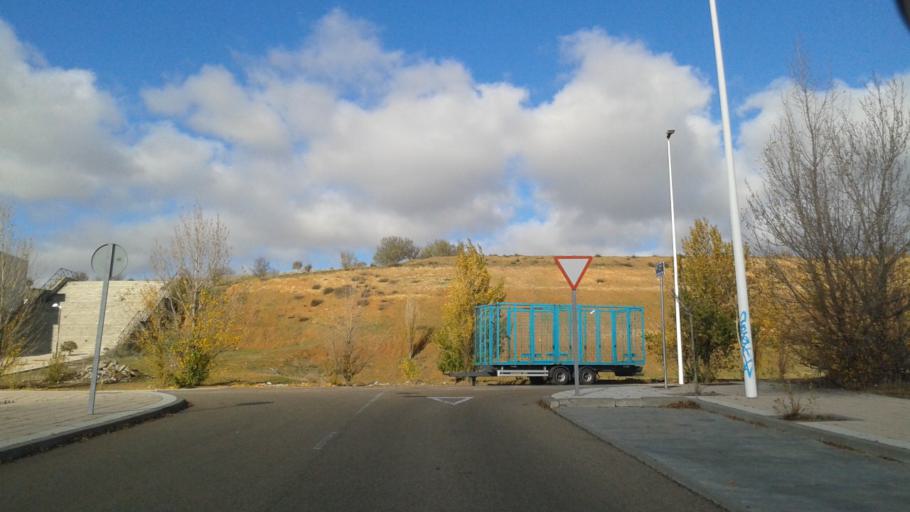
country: ES
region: Castille and Leon
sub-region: Provincia de Valladolid
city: Arroyo
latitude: 41.6275
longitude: -4.7639
